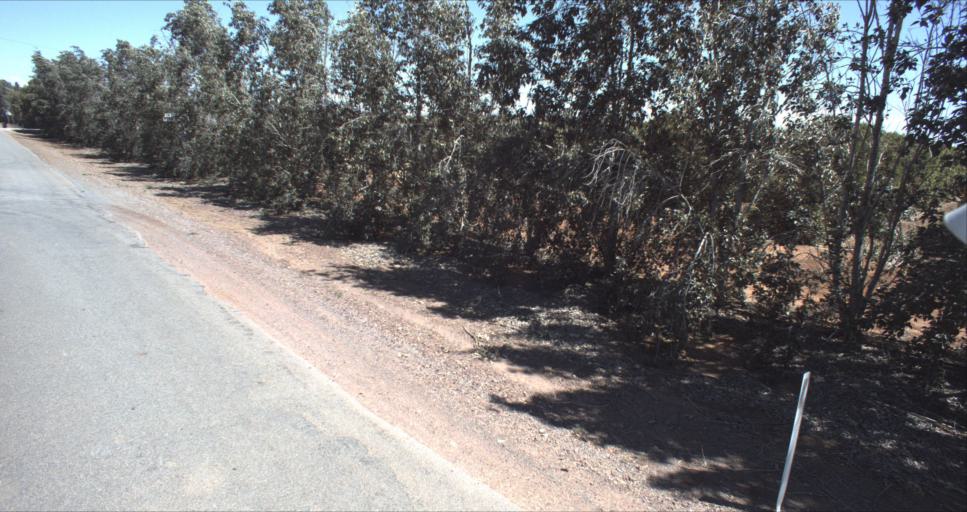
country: AU
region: New South Wales
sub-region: Leeton
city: Leeton
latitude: -34.5248
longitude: 146.3302
